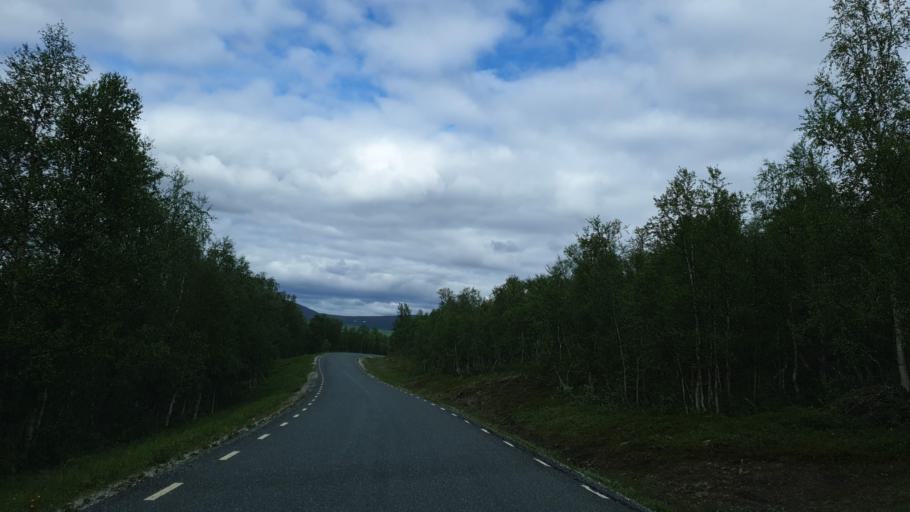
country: NO
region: Nordland
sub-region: Hattfjelldal
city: Hattfjelldal
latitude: 65.4220
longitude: 14.8810
